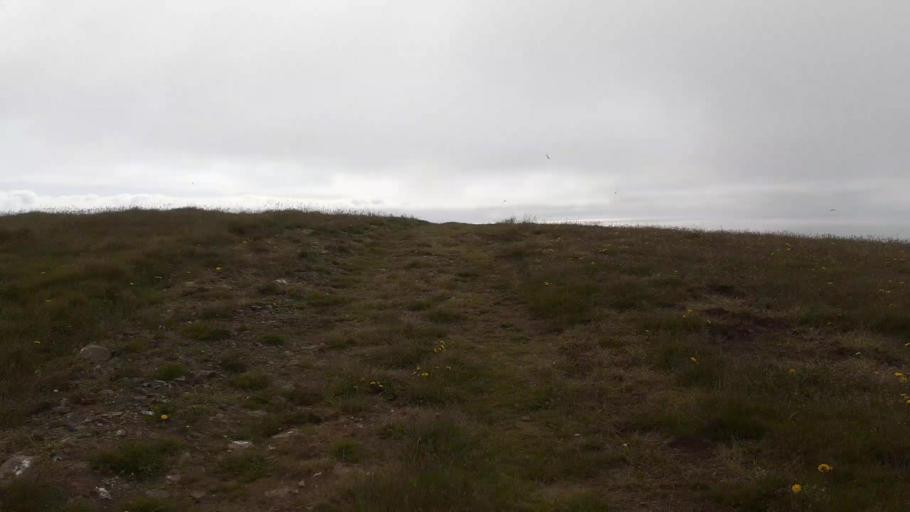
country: IS
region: Northeast
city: Dalvik
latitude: 66.5442
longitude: -18.0012
